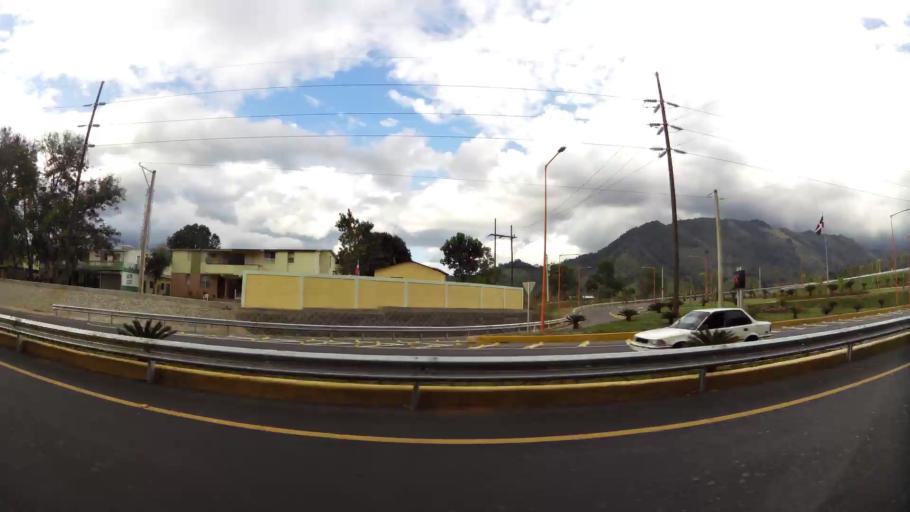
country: DO
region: Monsenor Nouel
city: Piedra Blanca
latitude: 18.8404
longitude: -70.3072
